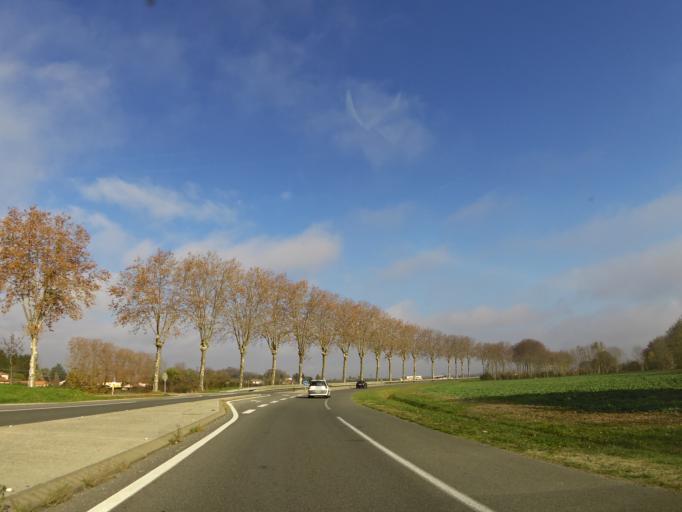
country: FR
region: Rhone-Alpes
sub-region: Departement de l'Ain
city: Meximieux
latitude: 45.9045
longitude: 5.2038
